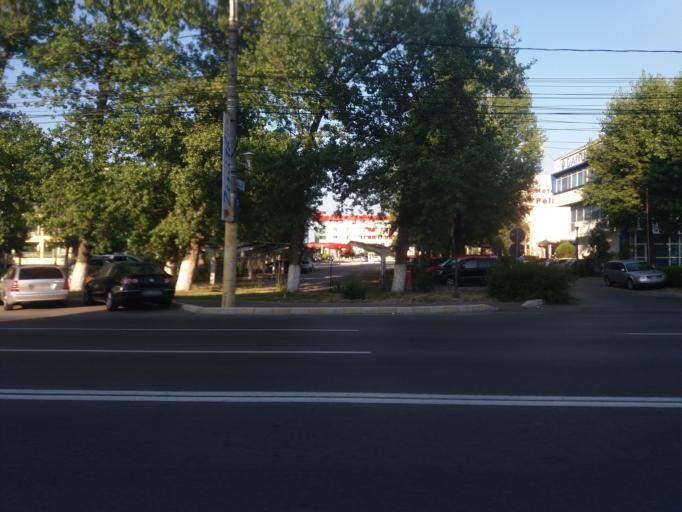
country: RO
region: Constanta
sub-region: Municipiul Constanta
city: Palazu Mare
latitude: 44.2540
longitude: 28.6188
